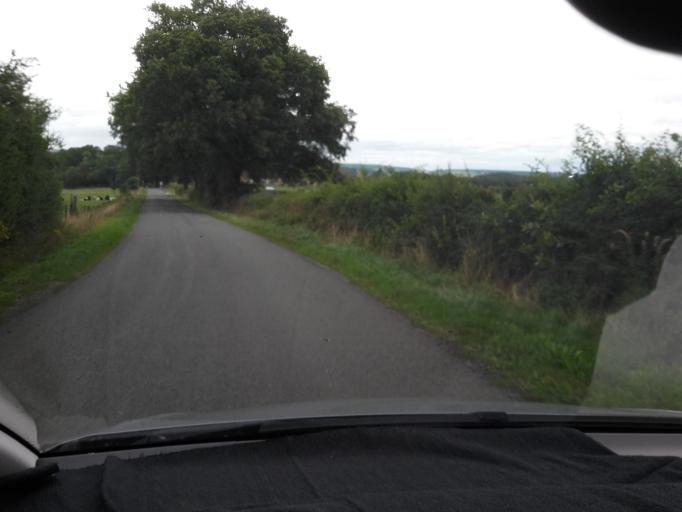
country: BE
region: Wallonia
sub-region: Province du Luxembourg
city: Attert
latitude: 49.7437
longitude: 5.8109
